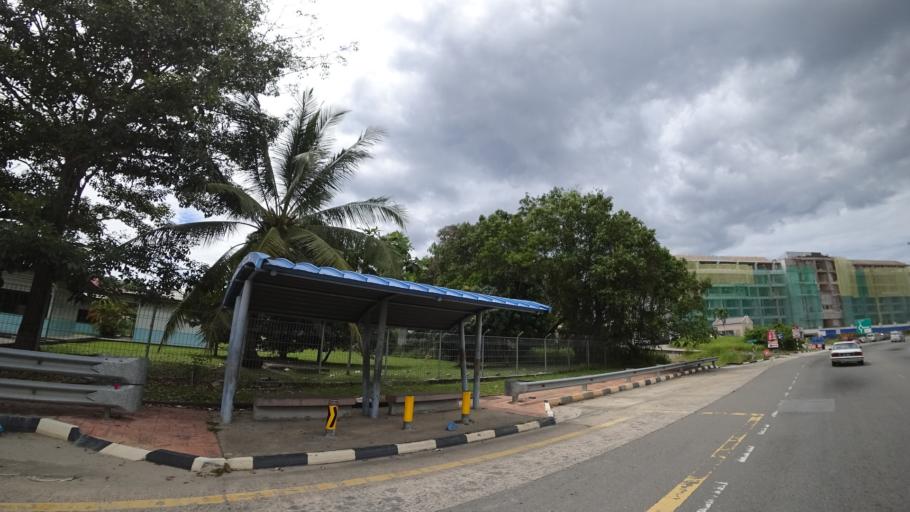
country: BN
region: Brunei and Muara
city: Bandar Seri Begawan
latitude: 4.8935
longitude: 114.8987
